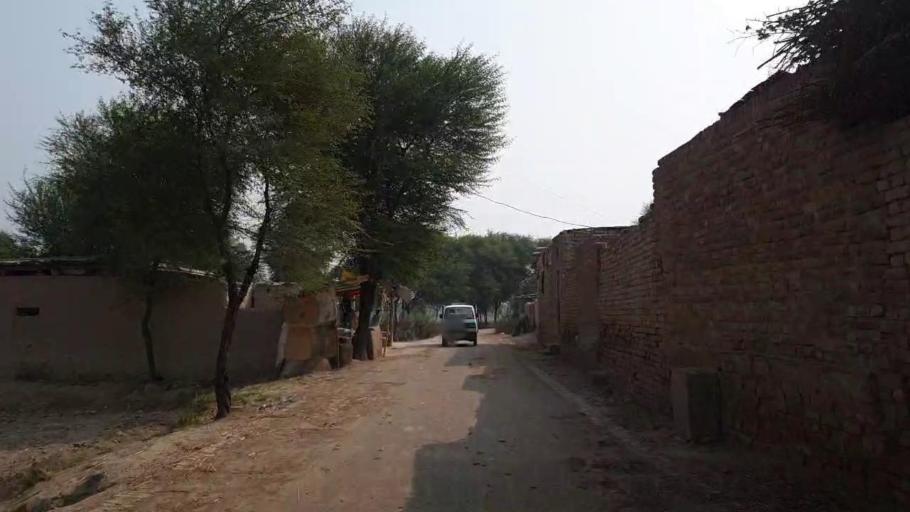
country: PK
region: Sindh
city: Tando Muhammad Khan
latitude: 25.1829
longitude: 68.6252
